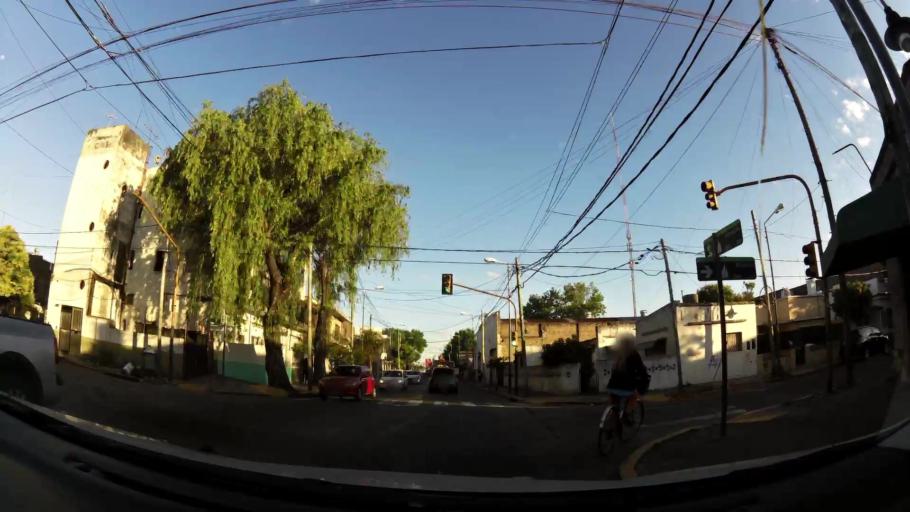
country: AR
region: Buenos Aires
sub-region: Partido de Tigre
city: Tigre
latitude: -34.4458
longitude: -58.5635
